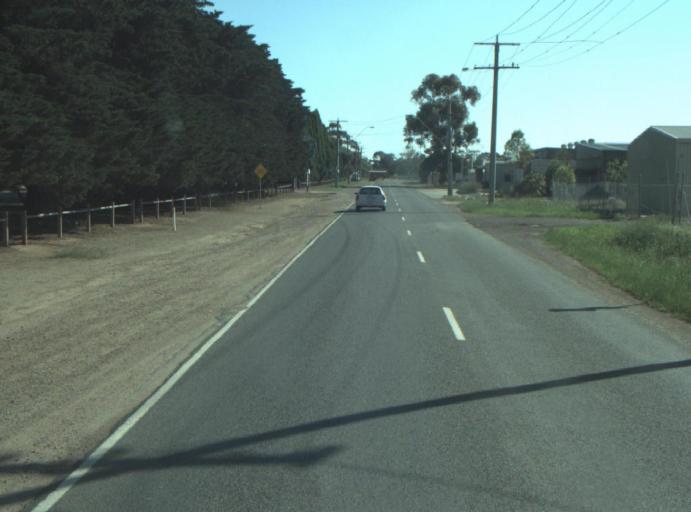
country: AU
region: Victoria
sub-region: Greater Geelong
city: Lara
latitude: -38.0216
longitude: 144.4132
